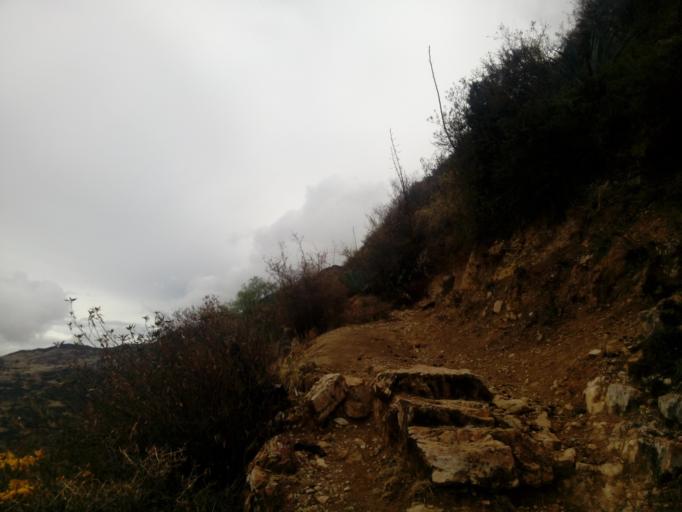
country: PE
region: Ayacucho
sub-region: Provincia de Victor Fajardo
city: Canaria
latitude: -13.8977
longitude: -73.9333
